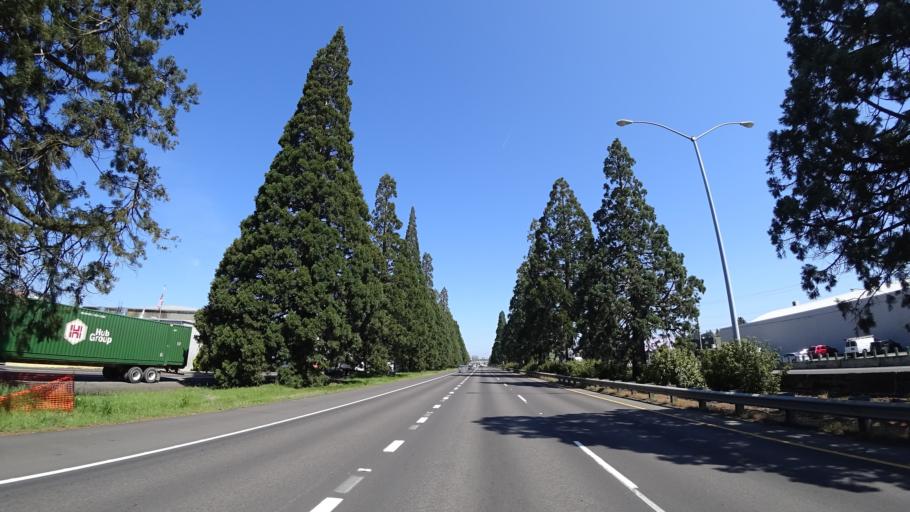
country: US
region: Oregon
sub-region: Clackamas County
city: Milwaukie
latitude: 45.4541
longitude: -122.6410
